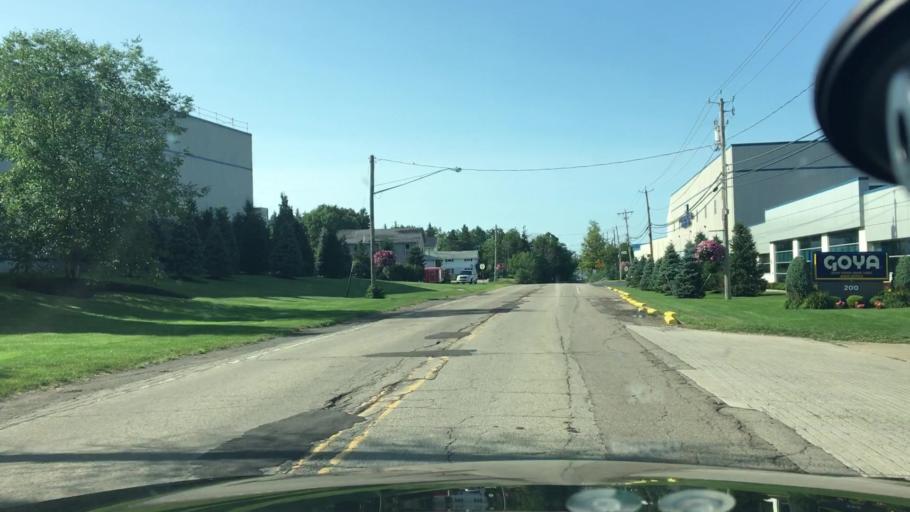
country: US
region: New York
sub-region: Erie County
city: Angola
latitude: 42.6288
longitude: -79.0271
